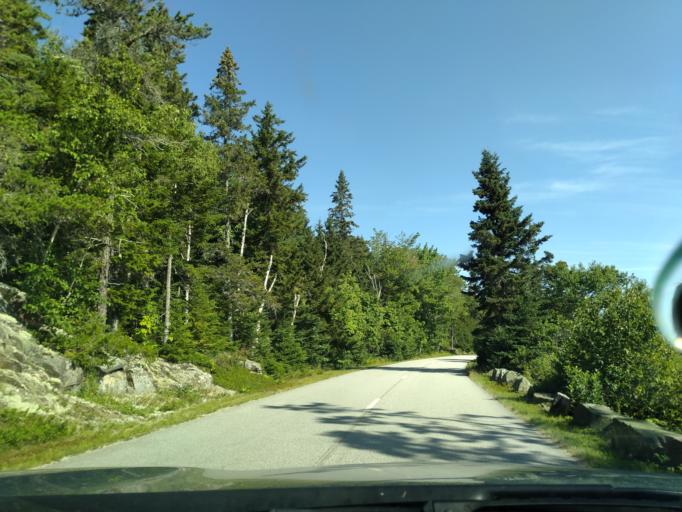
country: US
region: Maine
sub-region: Hancock County
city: Gouldsboro
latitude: 44.3576
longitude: -68.0469
